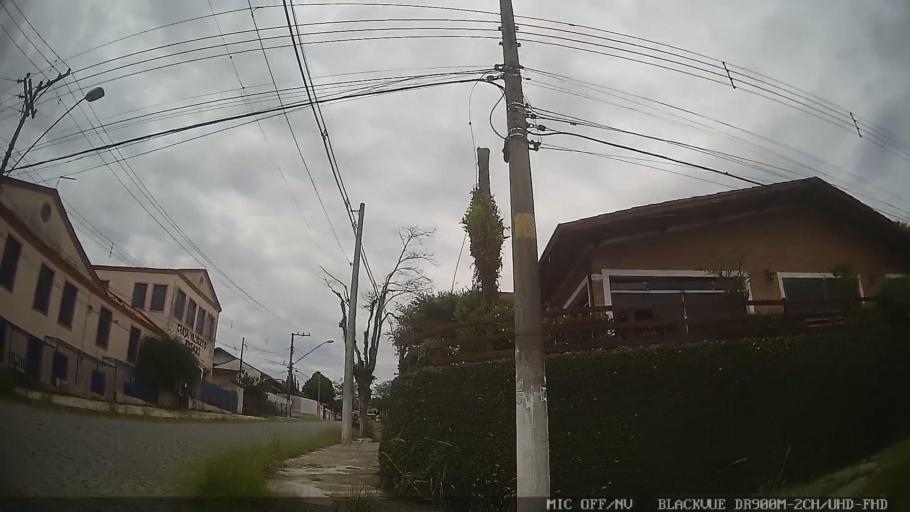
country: BR
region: Sao Paulo
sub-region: Ribeirao Pires
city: Ribeirao Pires
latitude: -23.7144
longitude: -46.4177
